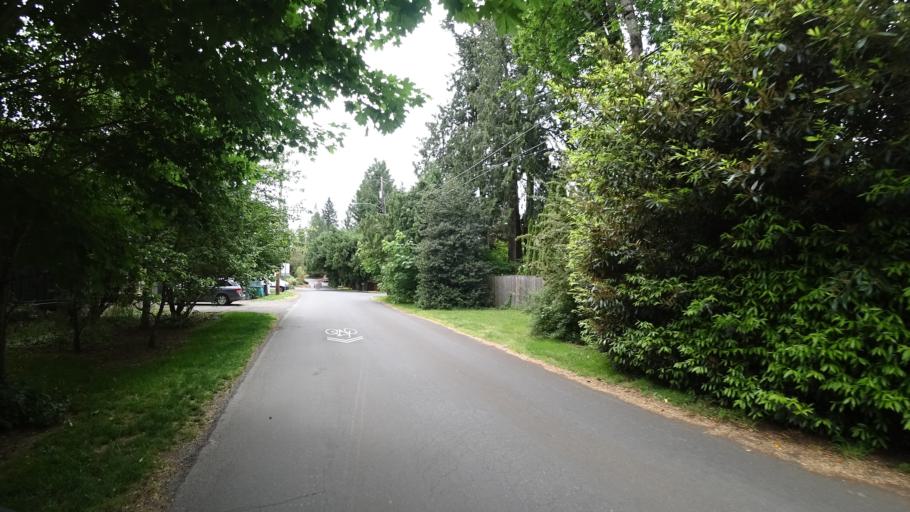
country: US
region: Oregon
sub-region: Washington County
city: Garden Home-Whitford
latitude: 45.4739
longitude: -122.7386
